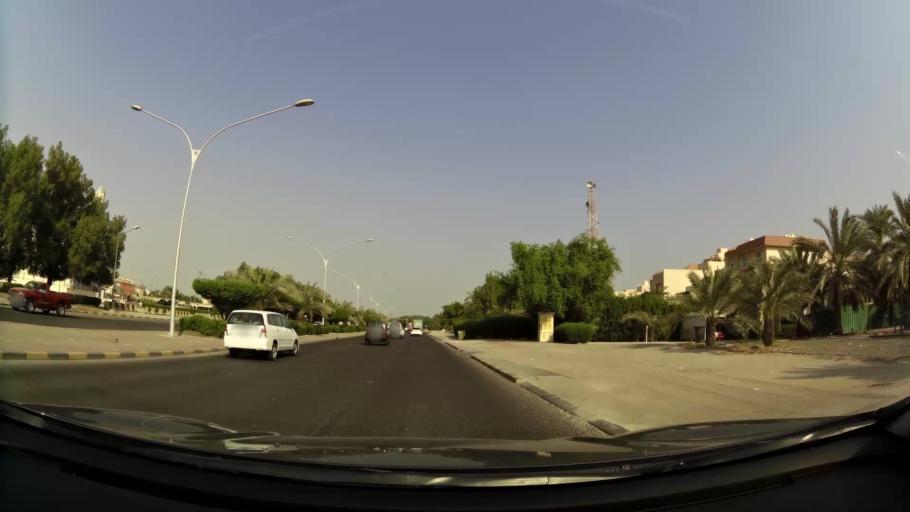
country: KW
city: Bayan
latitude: 29.2859
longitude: 48.0558
